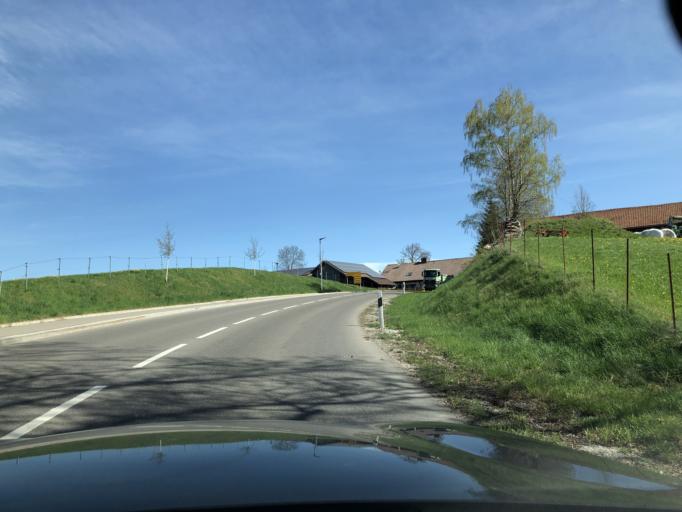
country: DE
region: Bavaria
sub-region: Swabia
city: Seeg
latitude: 47.6322
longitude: 10.5978
